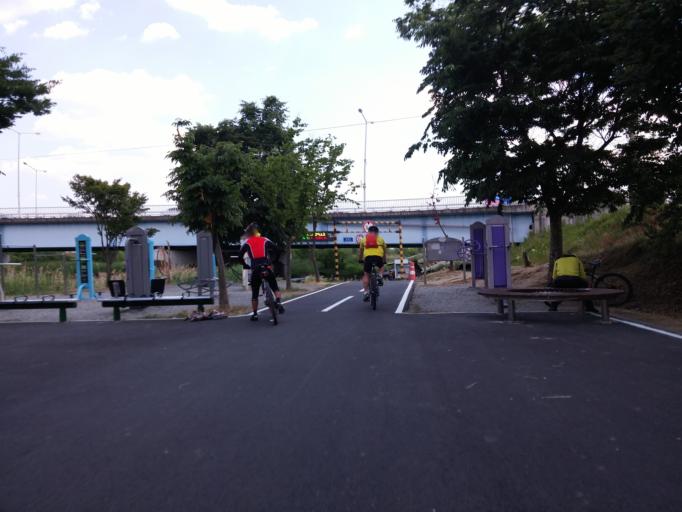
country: KR
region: Chungcheongbuk-do
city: Cheongju-si
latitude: 36.5969
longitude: 127.4969
